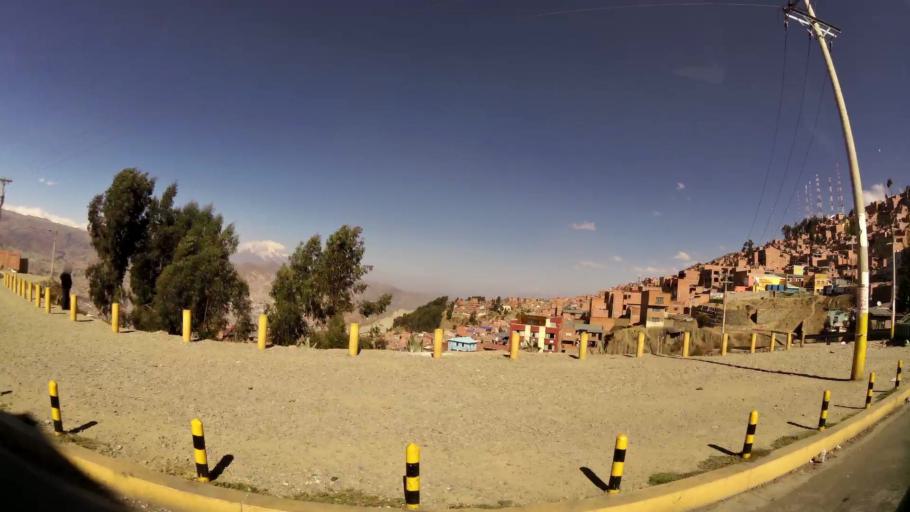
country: BO
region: La Paz
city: La Paz
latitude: -16.5211
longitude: -68.1457
